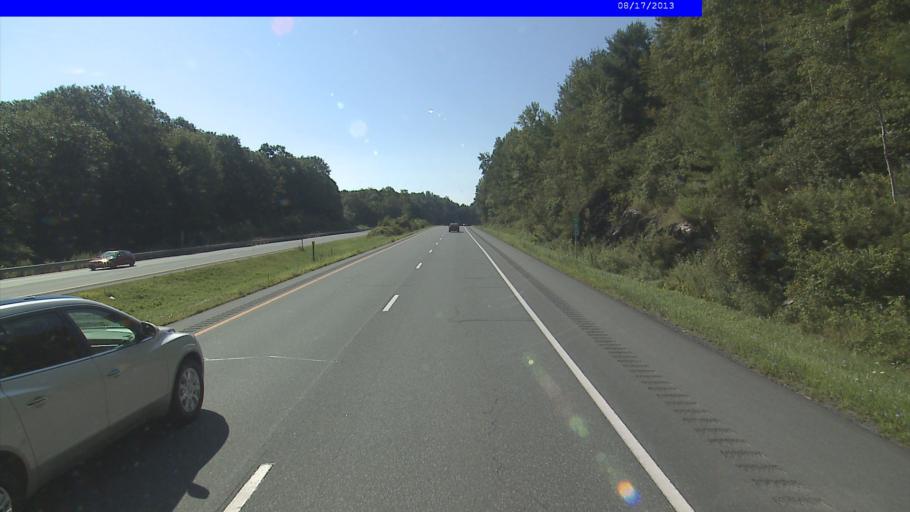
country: US
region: Vermont
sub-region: Windsor County
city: Windsor
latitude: 43.4953
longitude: -72.4099
